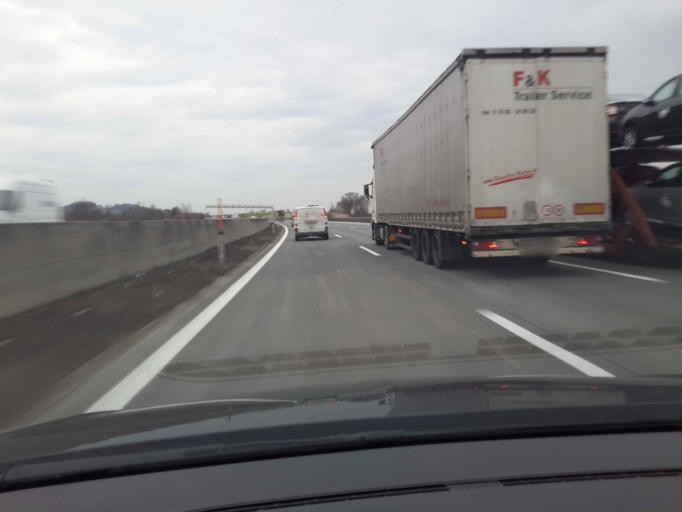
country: AT
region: Lower Austria
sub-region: Politischer Bezirk Melk
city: Leiben
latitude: 48.2154
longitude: 15.2931
